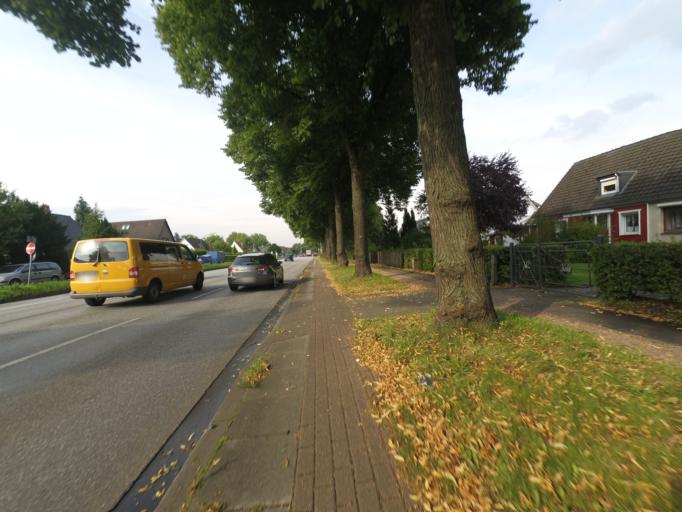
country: DE
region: Hamburg
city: Wandsbek
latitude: 53.5554
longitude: 10.1144
